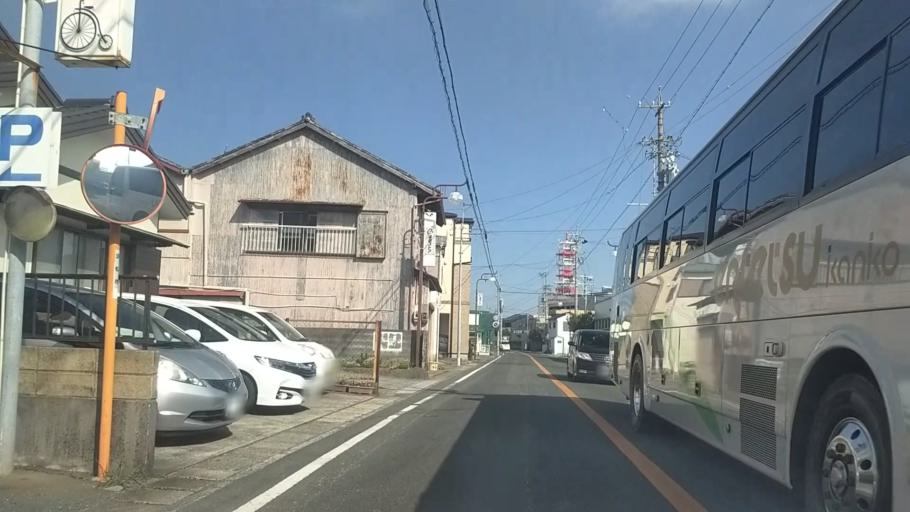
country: JP
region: Shizuoka
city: Hamamatsu
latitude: 34.7031
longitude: 137.7542
